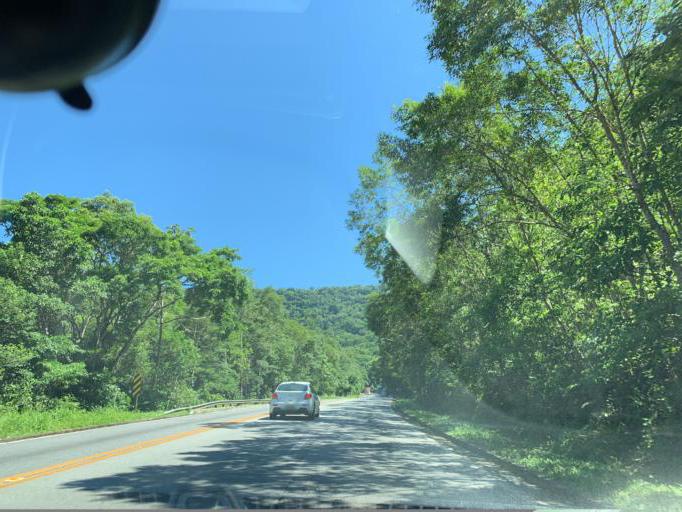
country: BR
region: Sao Paulo
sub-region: Bertioga
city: Bertioga
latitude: -23.7531
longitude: -46.0396
